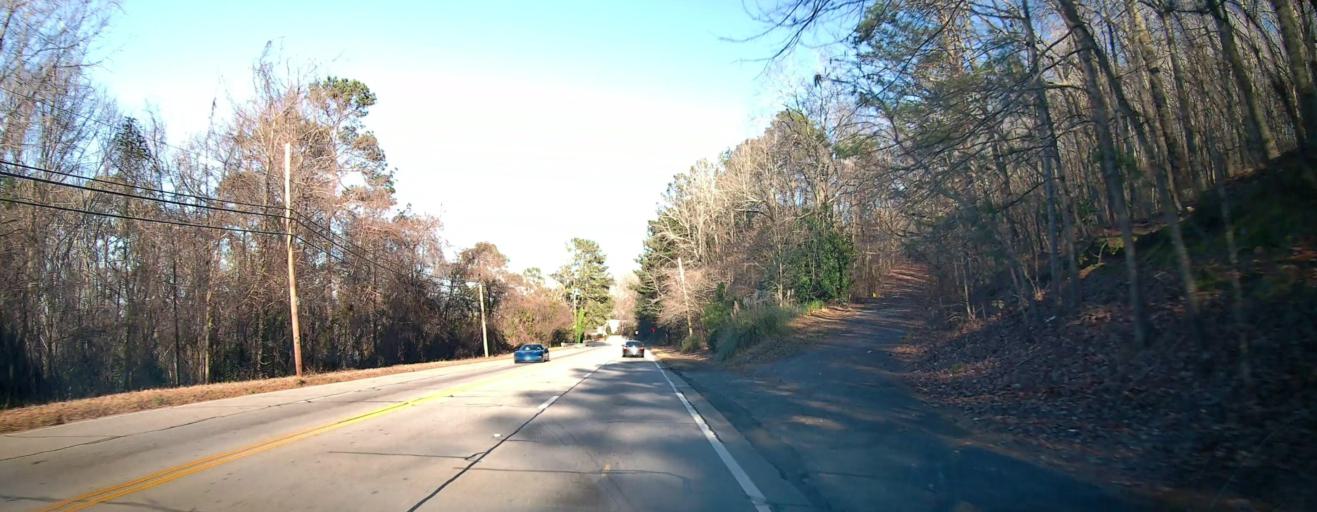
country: US
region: Georgia
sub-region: Meriwether County
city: Manchester
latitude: 32.8473
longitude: -84.6186
